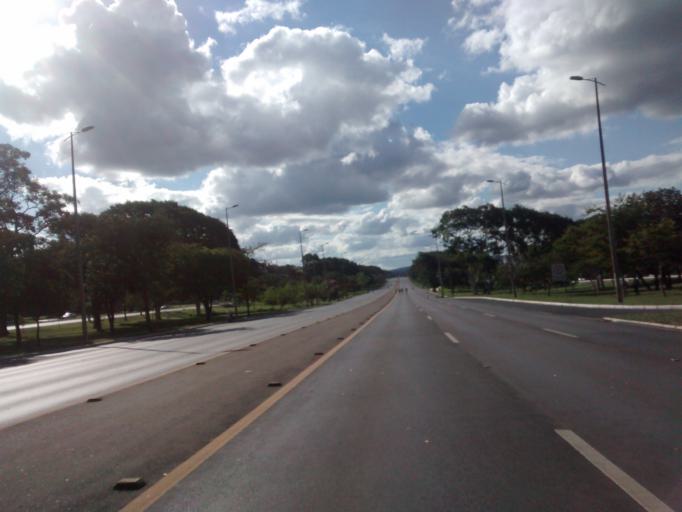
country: BR
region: Federal District
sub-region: Brasilia
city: Brasilia
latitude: -15.7539
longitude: -47.8868
